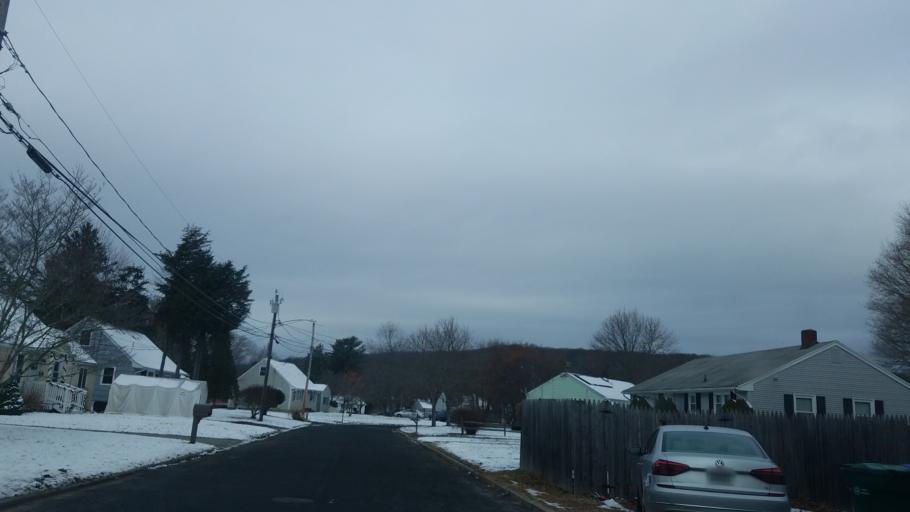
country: US
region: Connecticut
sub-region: New London County
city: Central Waterford
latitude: 41.3485
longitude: -72.1422
